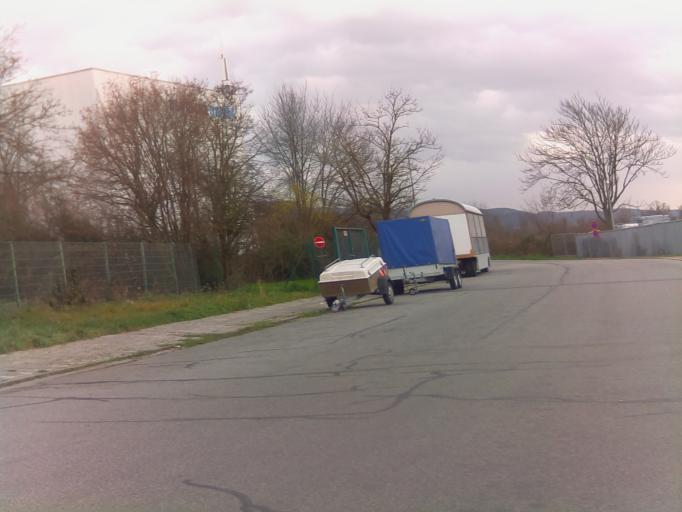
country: DE
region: Hesse
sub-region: Regierungsbezirk Darmstadt
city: Bensheim
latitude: 49.6672
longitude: 8.6100
